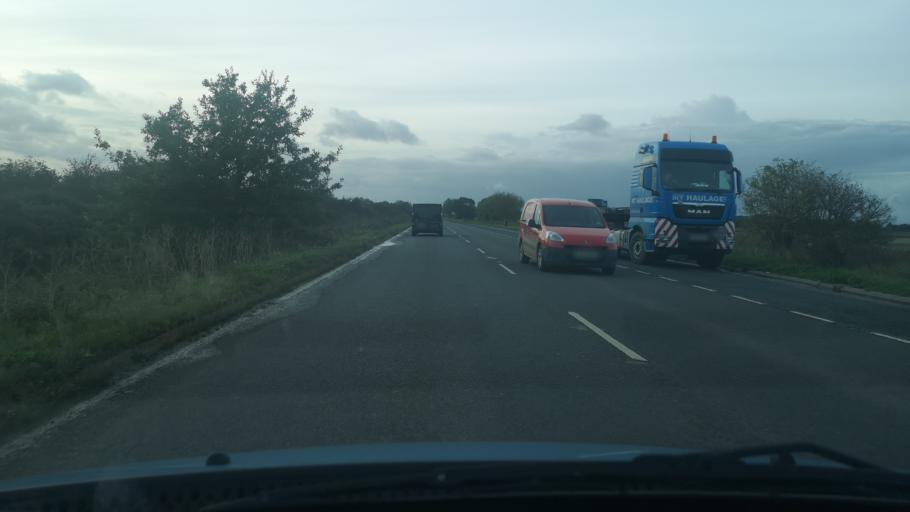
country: GB
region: England
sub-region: North Lincolnshire
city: Belton
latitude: 53.5812
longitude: -0.7940
